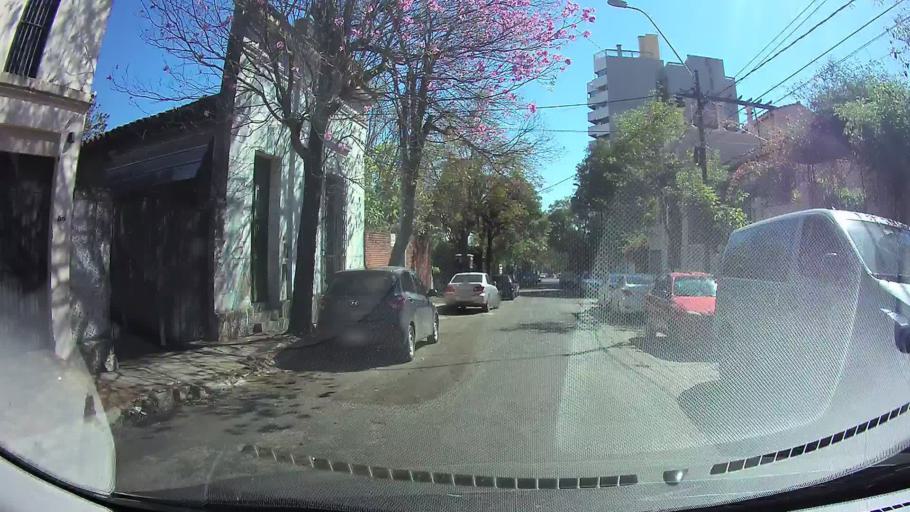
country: PY
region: Asuncion
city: Asuncion
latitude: -25.2842
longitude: -57.6181
